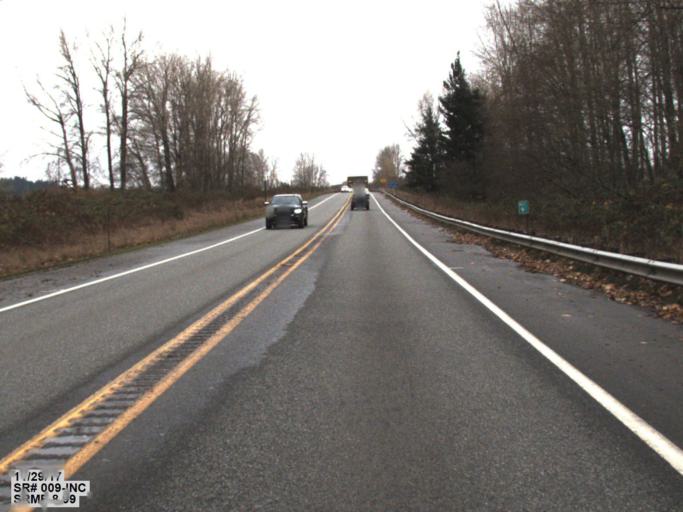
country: US
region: Washington
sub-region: Snohomish County
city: Snohomish
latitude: 47.9071
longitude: -122.1089
